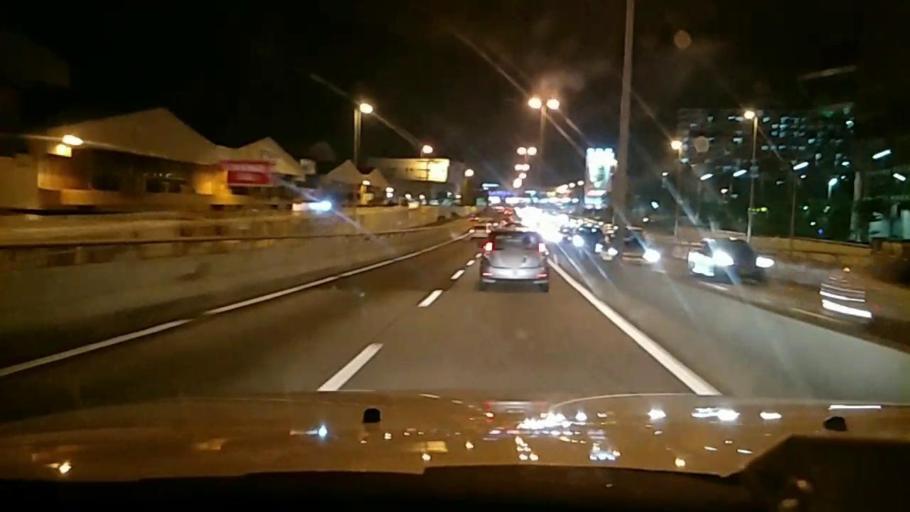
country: MY
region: Selangor
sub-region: Petaling
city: Petaling Jaya
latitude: 3.0867
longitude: 101.6131
